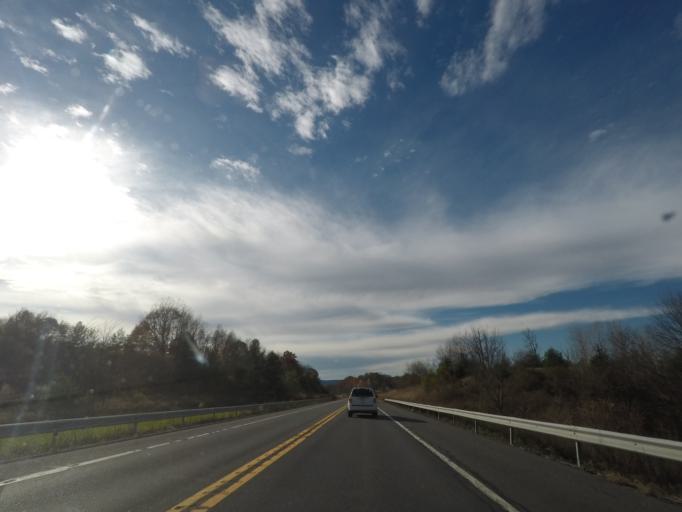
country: US
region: New York
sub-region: Albany County
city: McKownville
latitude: 42.6554
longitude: -73.8313
